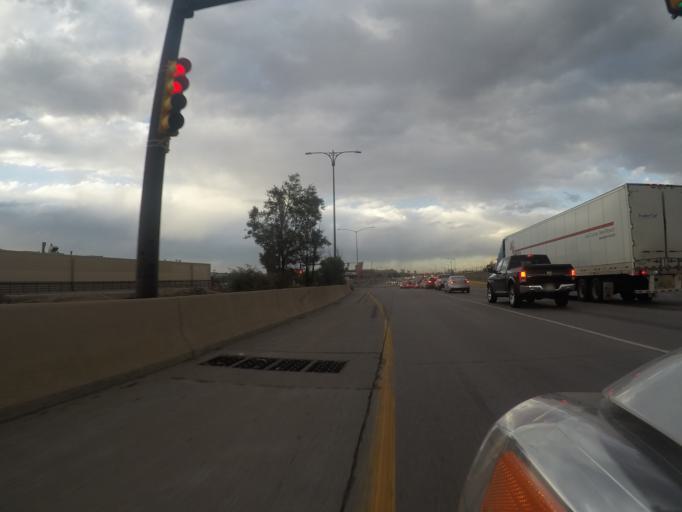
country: US
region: Colorado
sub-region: Arapahoe County
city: Sheridan
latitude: 39.6401
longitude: -105.0065
